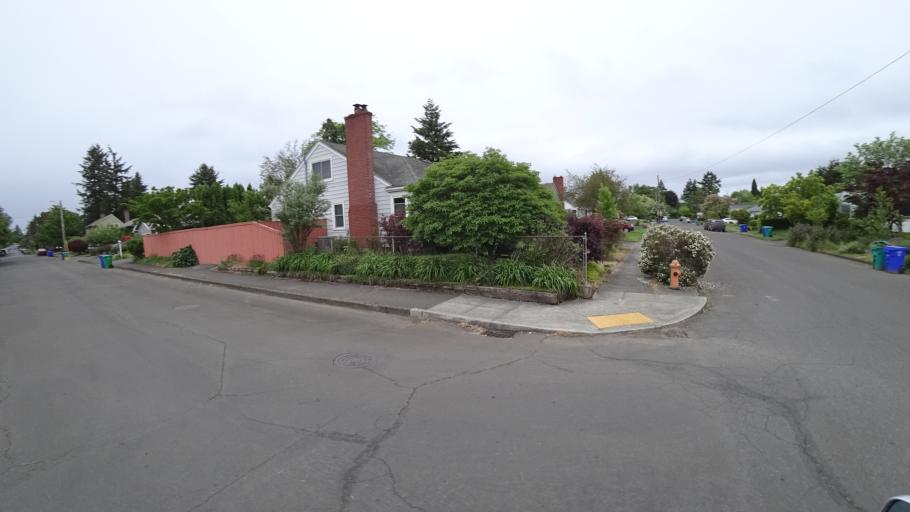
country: US
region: Oregon
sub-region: Multnomah County
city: Portland
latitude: 45.5595
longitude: -122.6234
